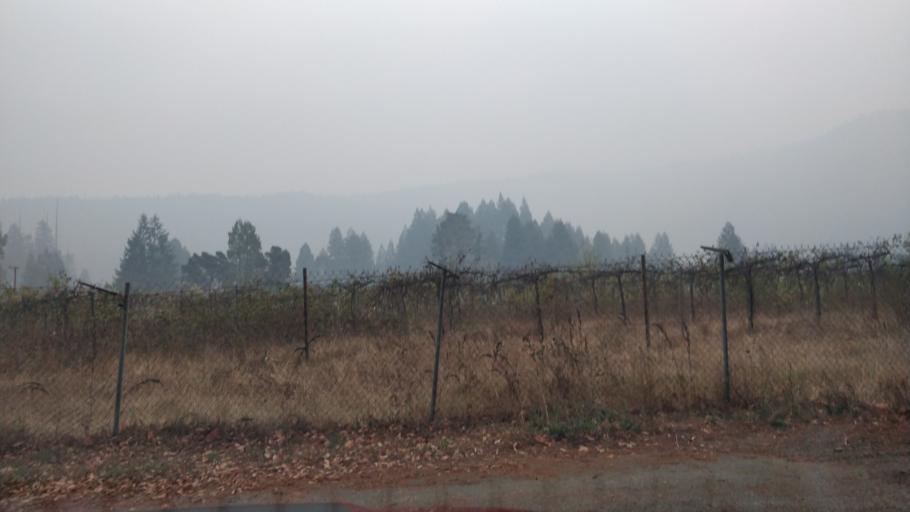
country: US
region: California
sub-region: Humboldt County
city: Redway
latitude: 40.2675
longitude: -123.8759
